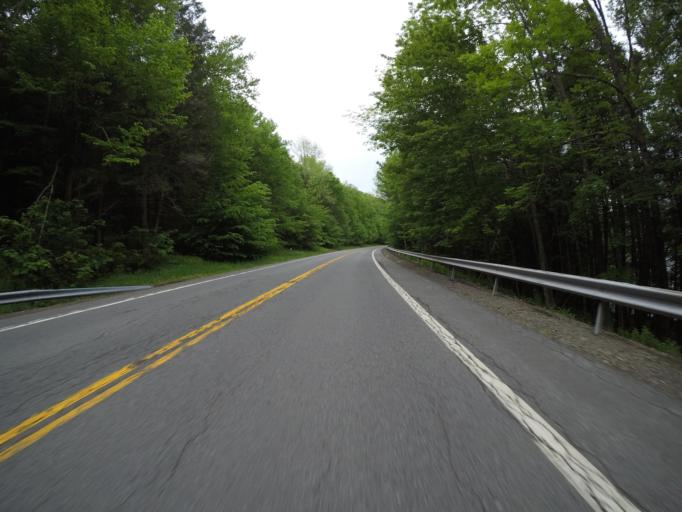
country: US
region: New York
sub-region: Sullivan County
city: Livingston Manor
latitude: 42.0733
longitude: -74.8693
